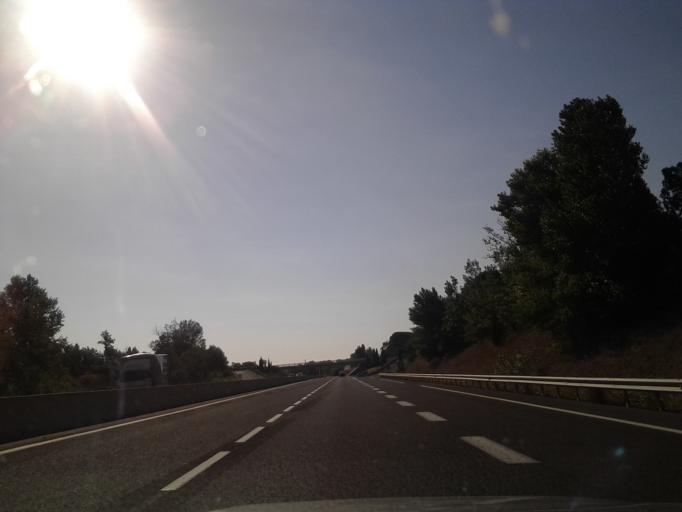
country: FR
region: Languedoc-Roussillon
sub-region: Departement des Pyrenees-Orientales
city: Corneilla-la-Riviere
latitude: 42.6837
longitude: 2.7457
